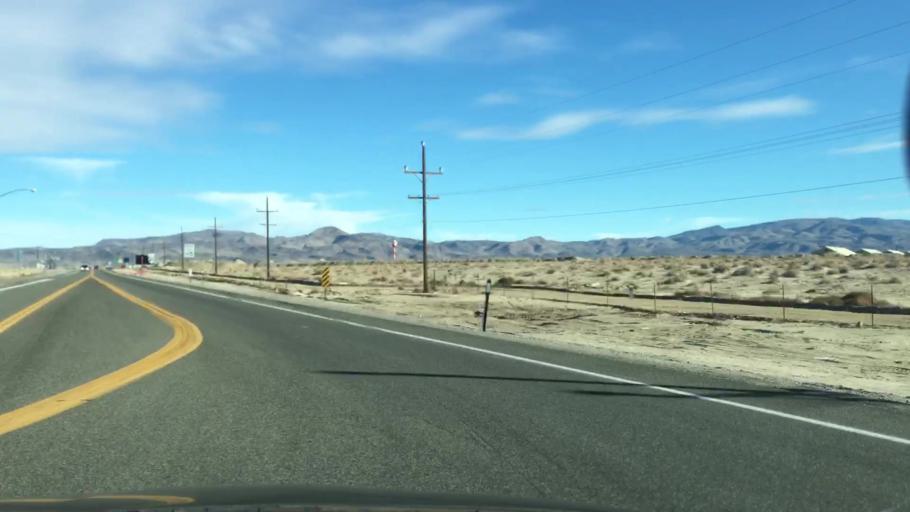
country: US
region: Nevada
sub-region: Mineral County
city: Hawthorne
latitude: 38.5245
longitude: -118.6108
